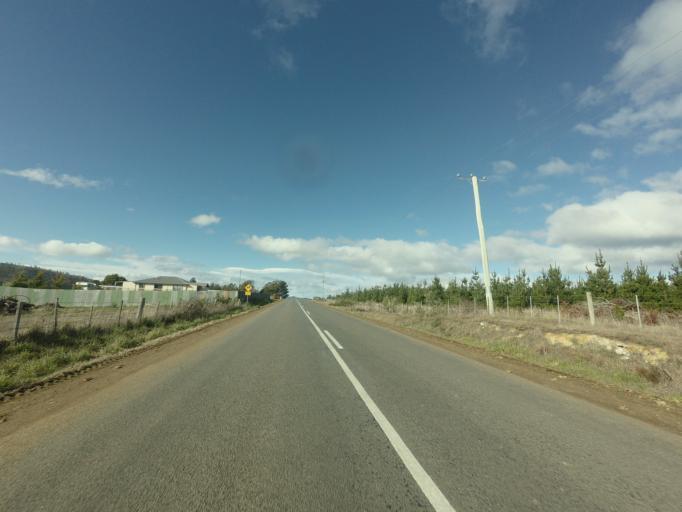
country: AU
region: Tasmania
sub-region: Derwent Valley
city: New Norfolk
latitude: -42.6834
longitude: 146.8226
